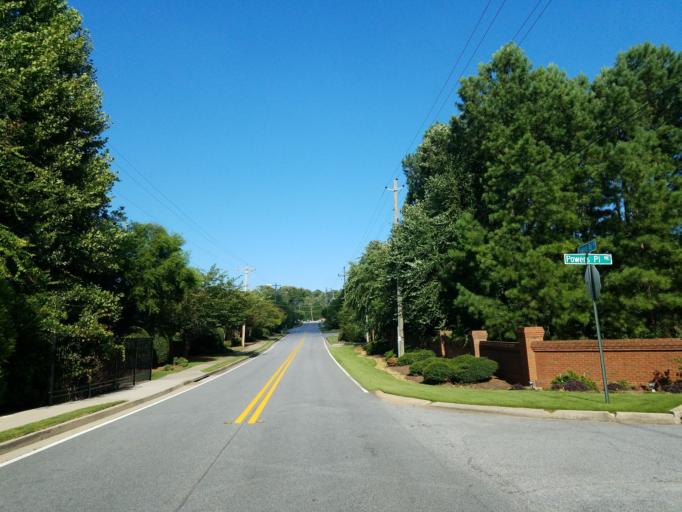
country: US
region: Georgia
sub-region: Fulton County
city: Sandy Springs
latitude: 33.9561
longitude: -84.4156
